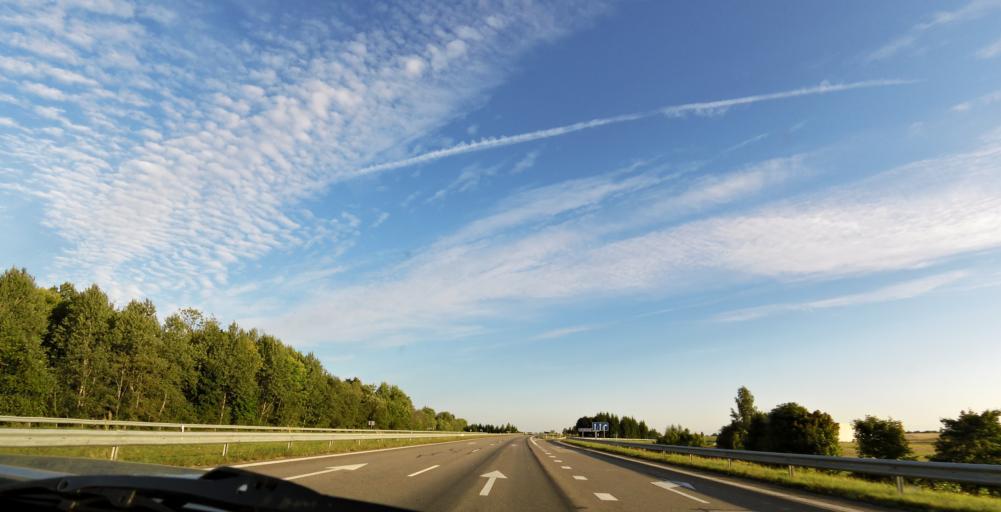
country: LT
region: Vilnius County
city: Ukmerge
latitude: 55.1754
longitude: 24.8129
